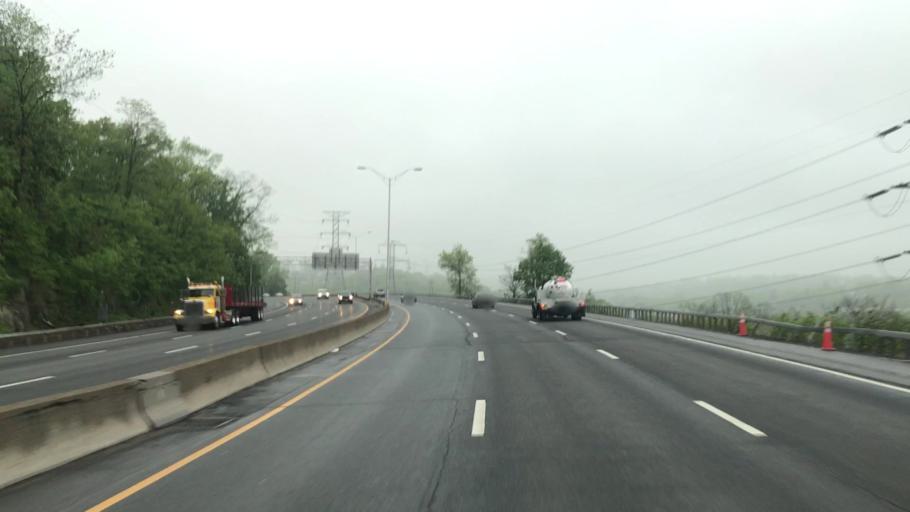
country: US
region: New York
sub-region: Westchester County
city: Bronxville
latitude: 40.9464
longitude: -73.8539
